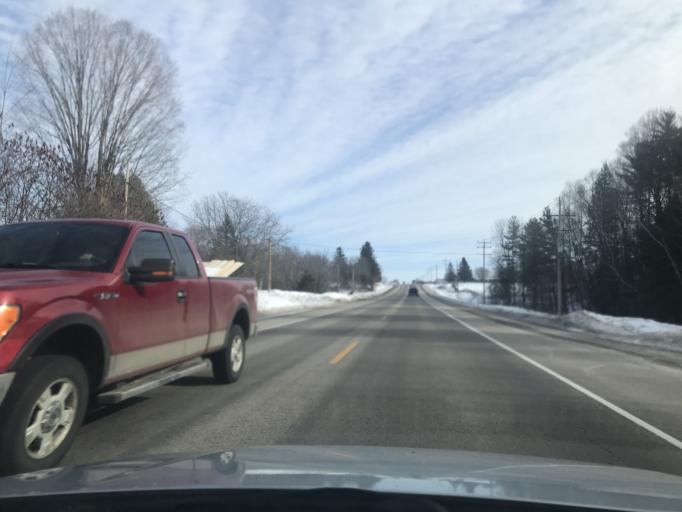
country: US
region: Wisconsin
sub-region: Oconto County
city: Gillett
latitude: 44.8964
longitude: -88.2838
